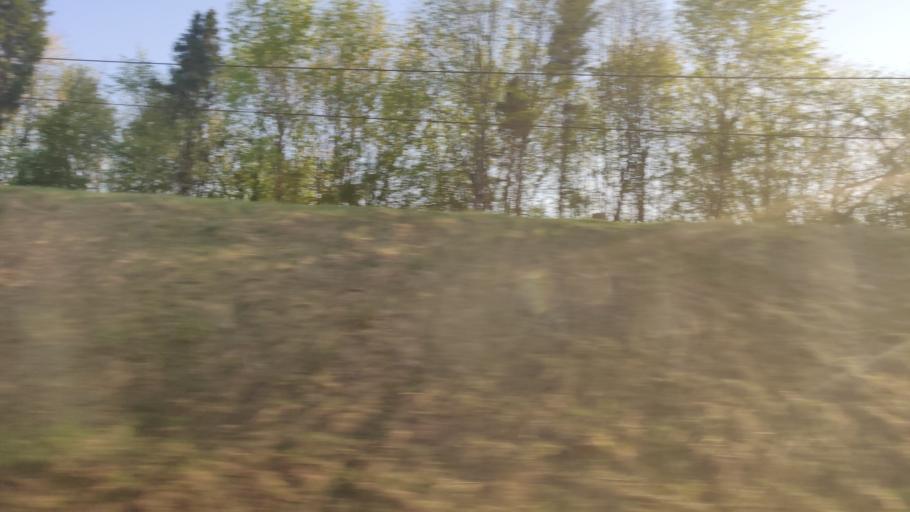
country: LT
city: Lentvaris
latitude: 54.6354
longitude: 25.0905
